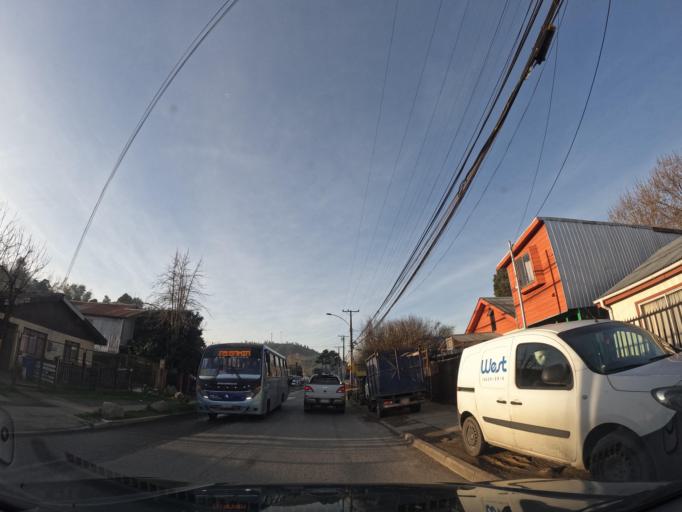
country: CL
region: Biobio
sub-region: Provincia de Concepcion
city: Concepcion
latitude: -36.8370
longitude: -73.0036
